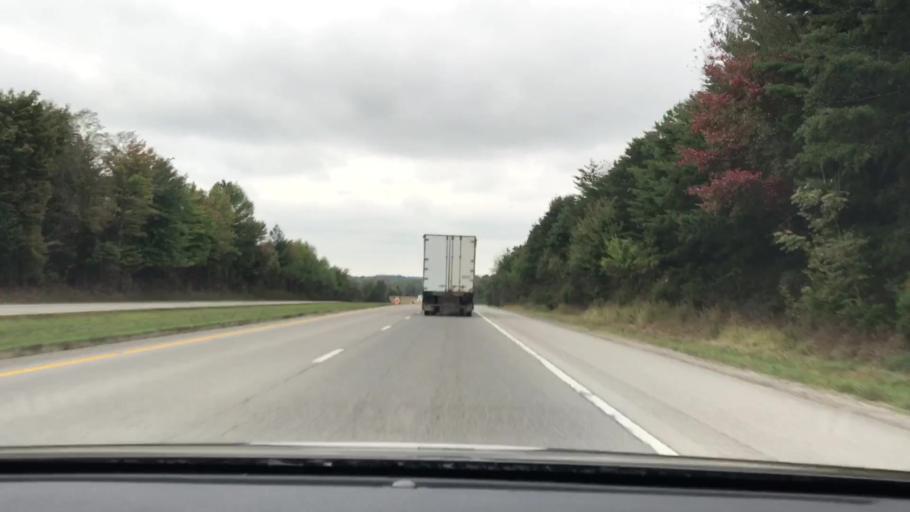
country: US
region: Kentucky
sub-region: Metcalfe County
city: Edmonton
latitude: 36.9972
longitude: -85.7068
